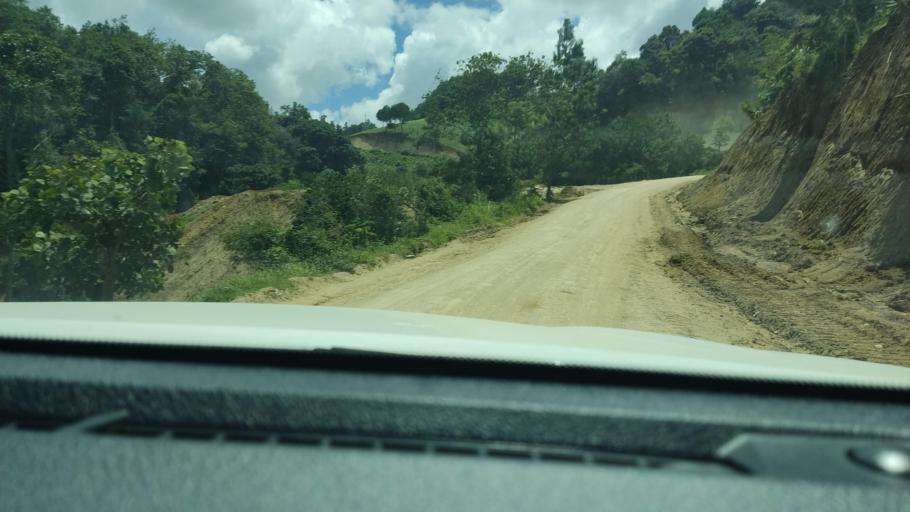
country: GT
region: Chimaltenango
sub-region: Municipio de San Juan Comalapa
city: Comalapa
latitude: 14.7711
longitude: -90.8779
